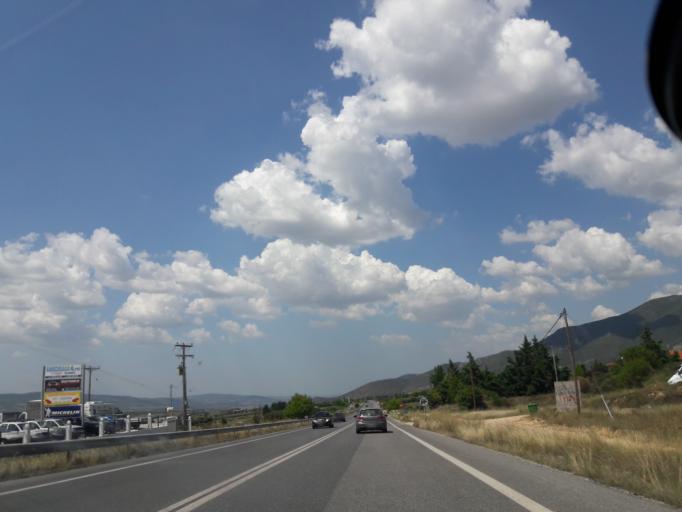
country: GR
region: Central Macedonia
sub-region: Nomos Chalkidikis
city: Galatista
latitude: 40.4644
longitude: 23.2649
